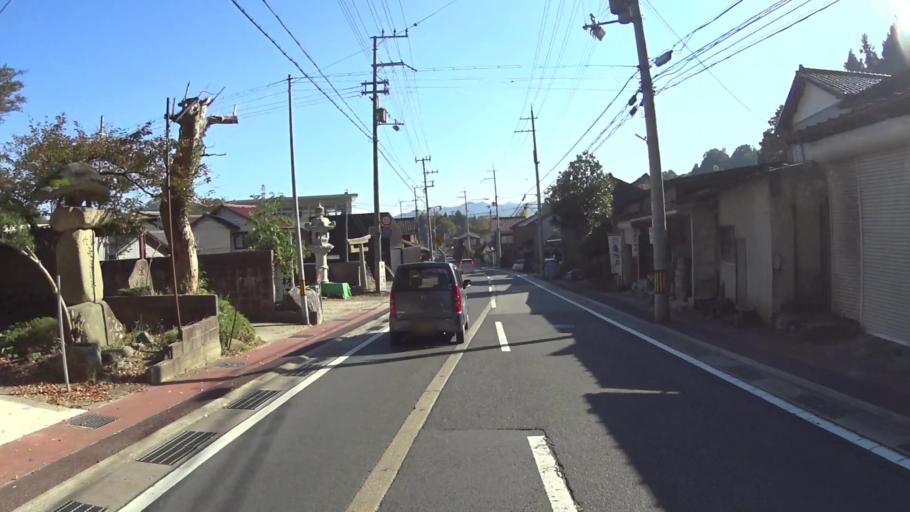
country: JP
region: Kyoto
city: Miyazu
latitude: 35.6306
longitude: 135.0552
